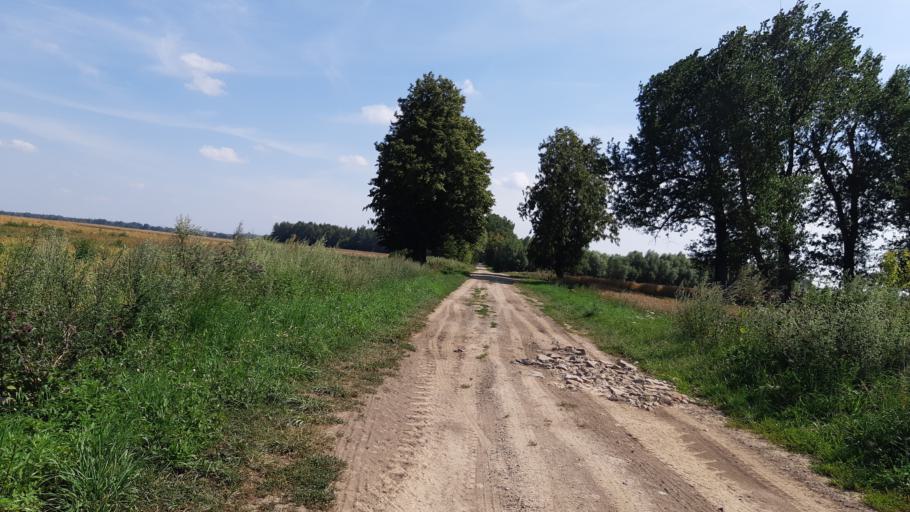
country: LT
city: Virbalis
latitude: 54.6403
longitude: 22.8208
